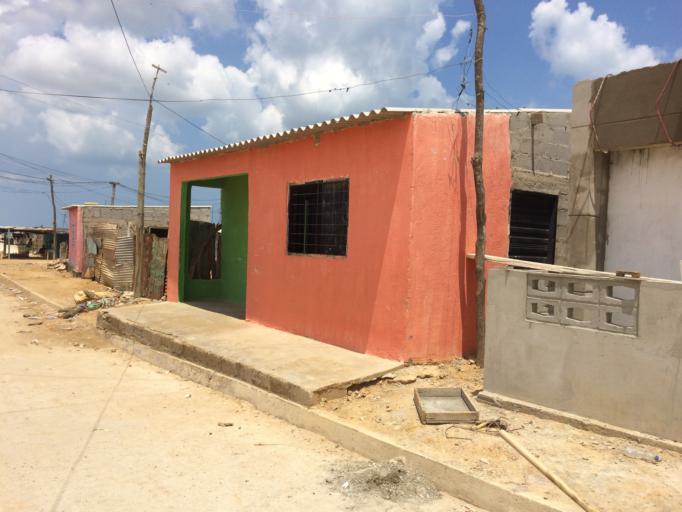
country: CO
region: La Guajira
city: Manaure
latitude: 11.7728
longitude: -72.4482
